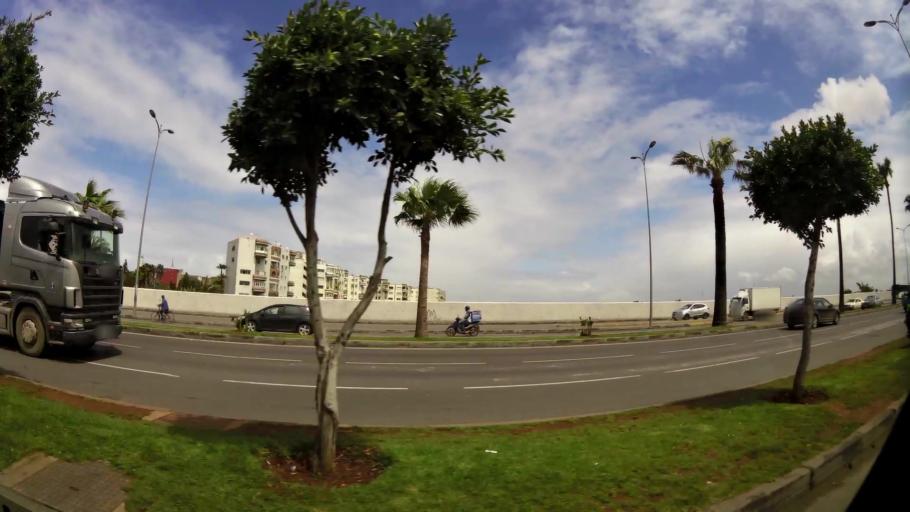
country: MA
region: Grand Casablanca
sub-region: Casablanca
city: Casablanca
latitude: 33.5755
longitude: -7.5854
